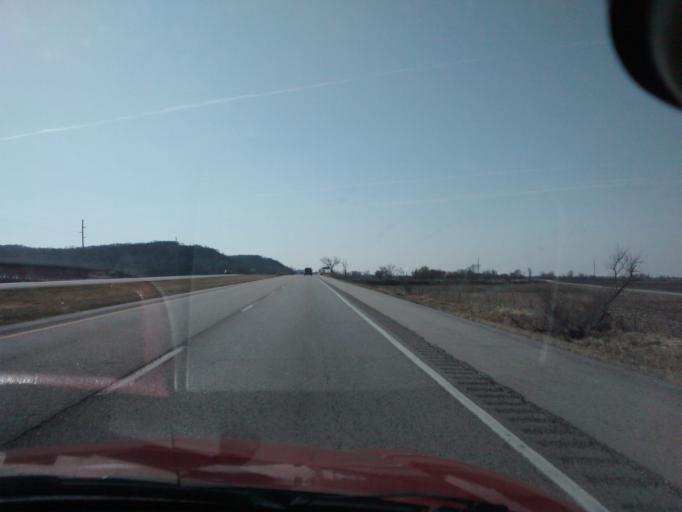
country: US
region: Iowa
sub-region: Pottawattamie County
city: Carter Lake
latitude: 41.3392
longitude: -95.8902
